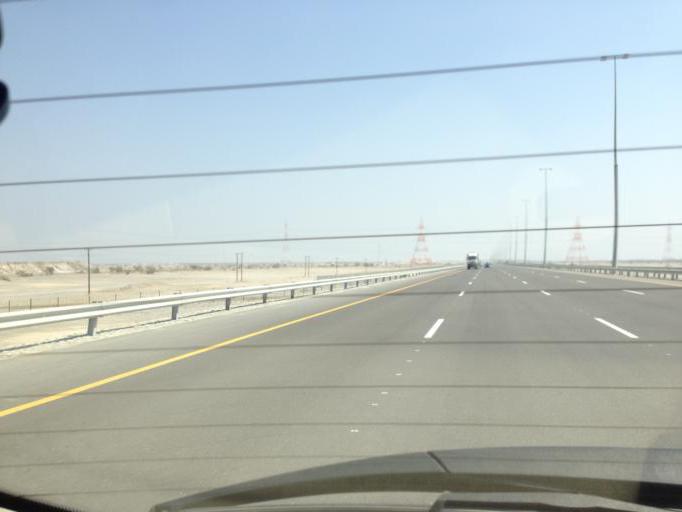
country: OM
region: Al Batinah
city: Barka'
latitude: 23.6076
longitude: 57.8252
